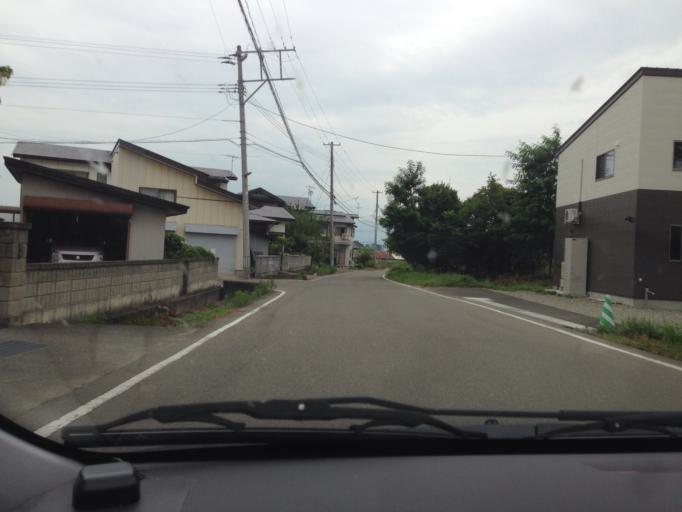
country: JP
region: Fukushima
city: Kitakata
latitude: 37.4644
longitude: 139.8487
